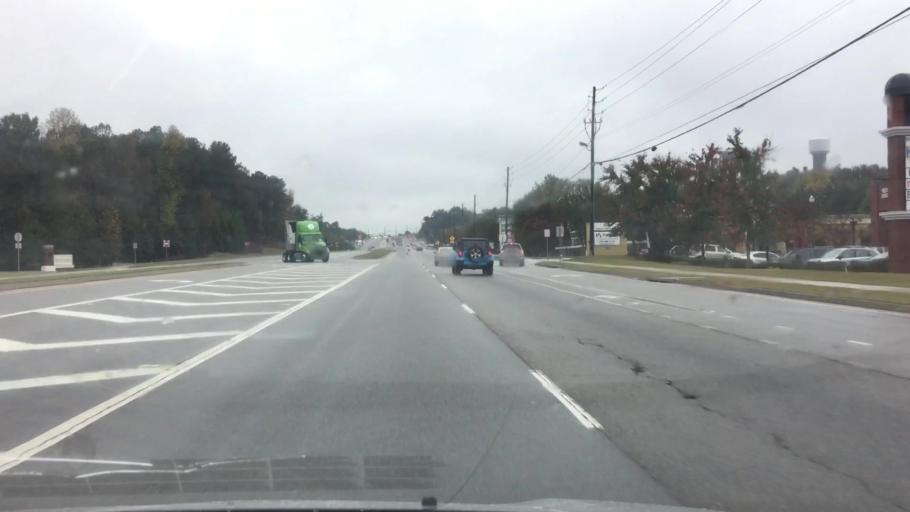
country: US
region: Georgia
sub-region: Henry County
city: Stockbridge
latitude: 33.5138
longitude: -84.2114
